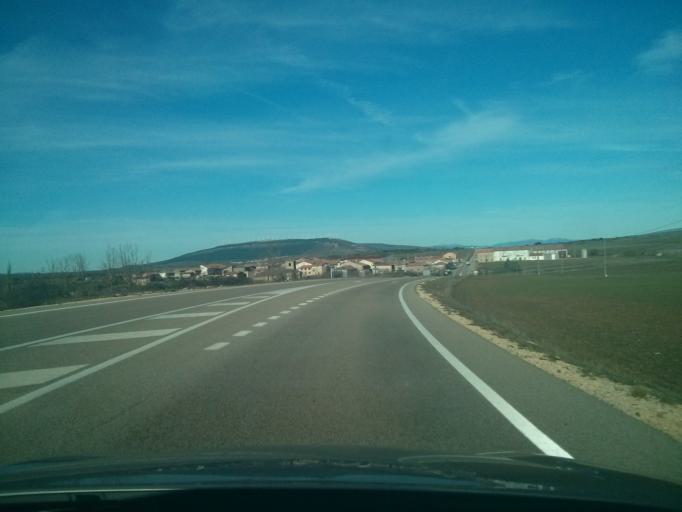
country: ES
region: Castille and Leon
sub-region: Provincia de Burgos
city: Rucandio
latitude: 42.7652
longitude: -3.6163
